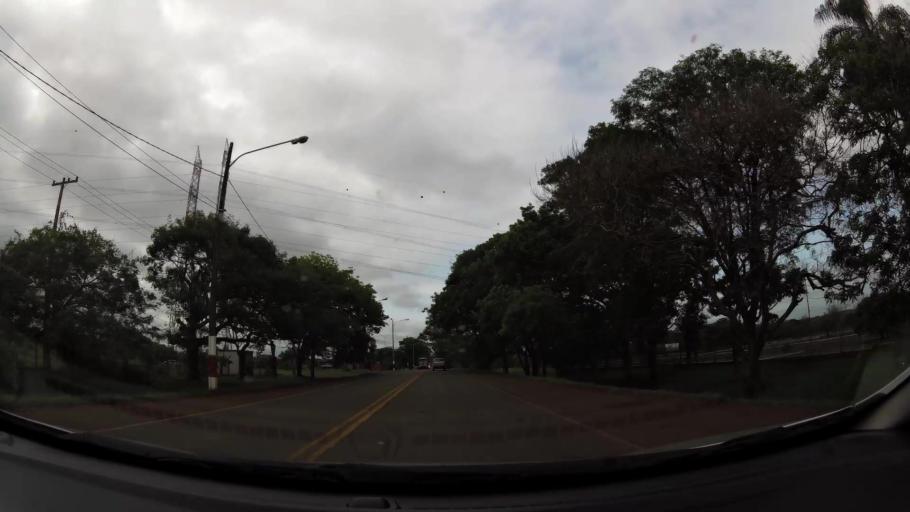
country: PY
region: Alto Parana
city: Ciudad del Este
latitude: -25.4281
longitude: -54.6385
